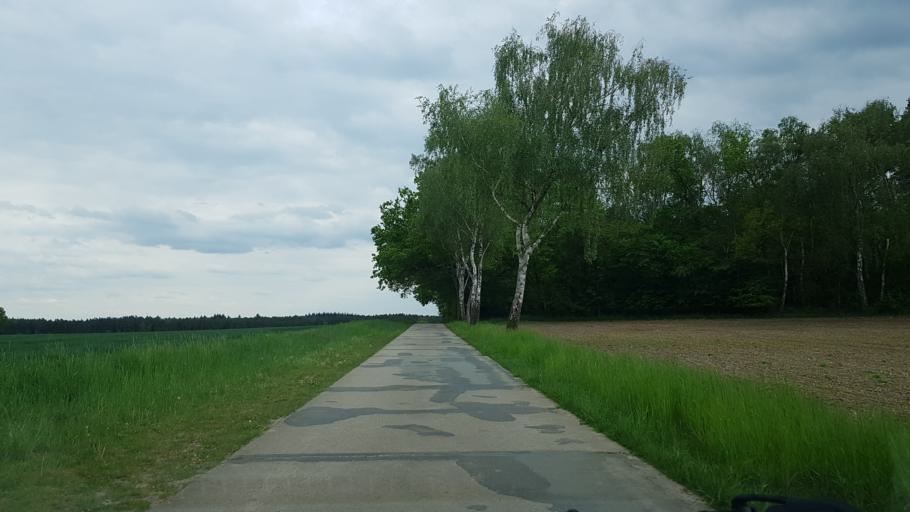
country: DE
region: Lower Saxony
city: Vastorf
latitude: 53.1824
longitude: 10.5518
